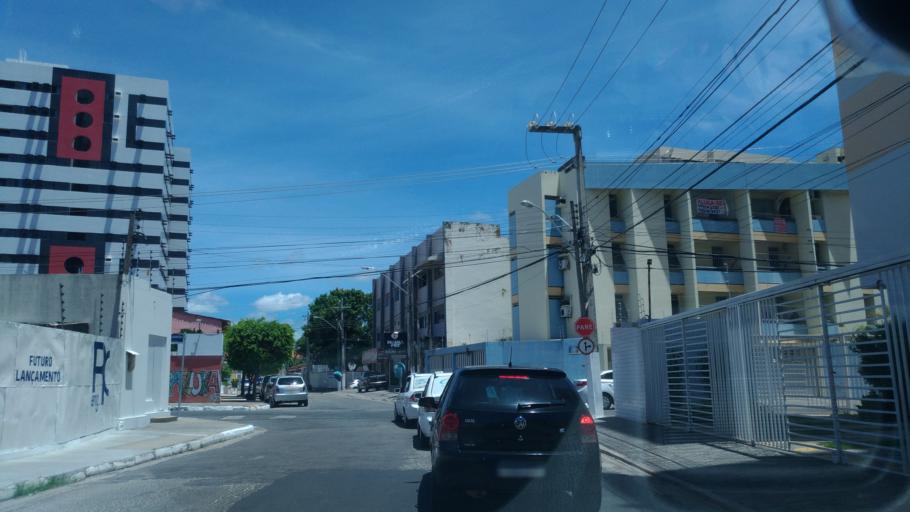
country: BR
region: Alagoas
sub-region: Maceio
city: Maceio
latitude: -9.6604
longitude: -35.7117
